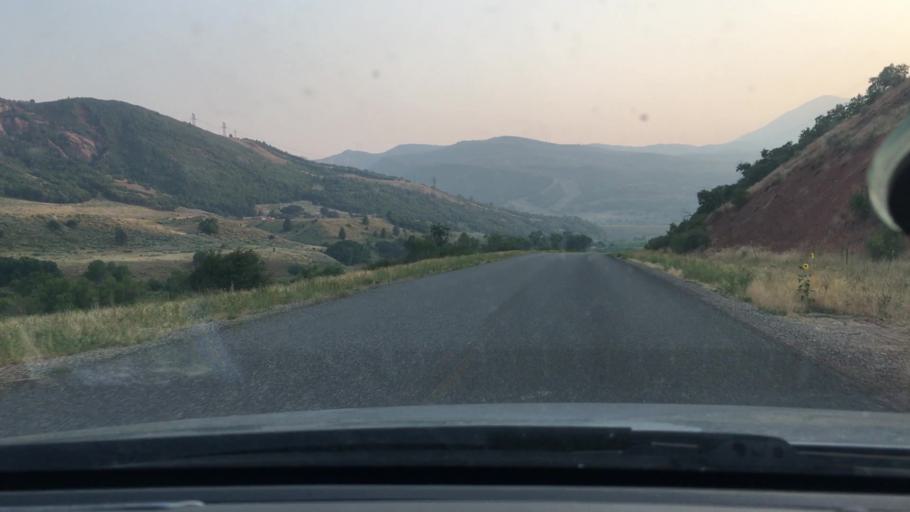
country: US
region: Utah
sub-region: Utah County
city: Mapleton
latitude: 40.0395
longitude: -111.4892
